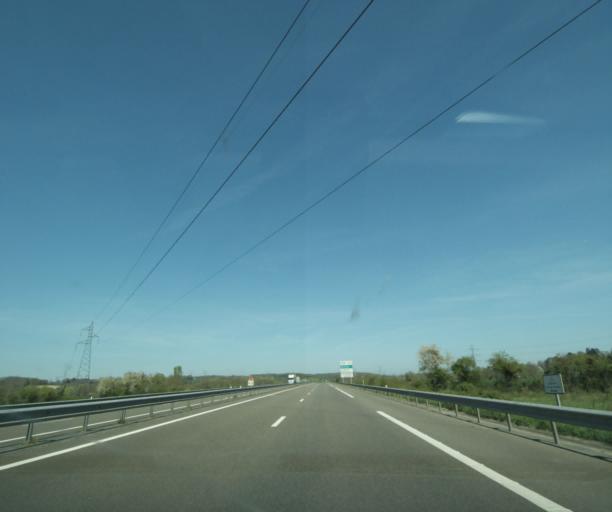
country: FR
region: Bourgogne
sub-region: Departement de la Nievre
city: Coulanges-les-Nevers
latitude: 46.9983
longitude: 3.2055
